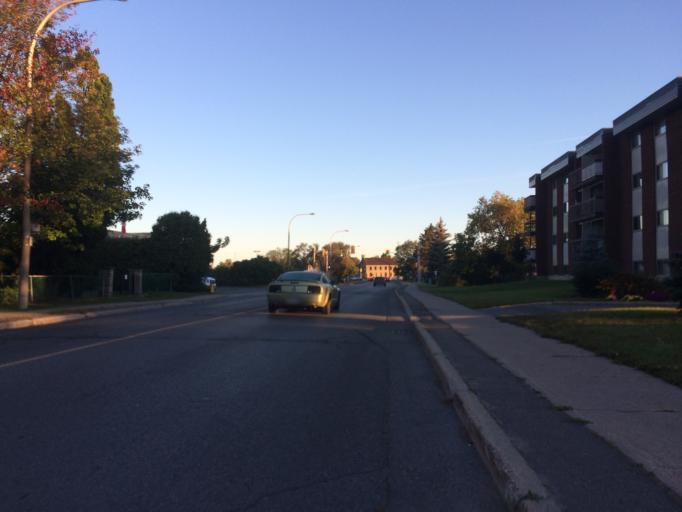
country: CA
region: Ontario
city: Bells Corners
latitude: 45.3226
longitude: -75.8260
